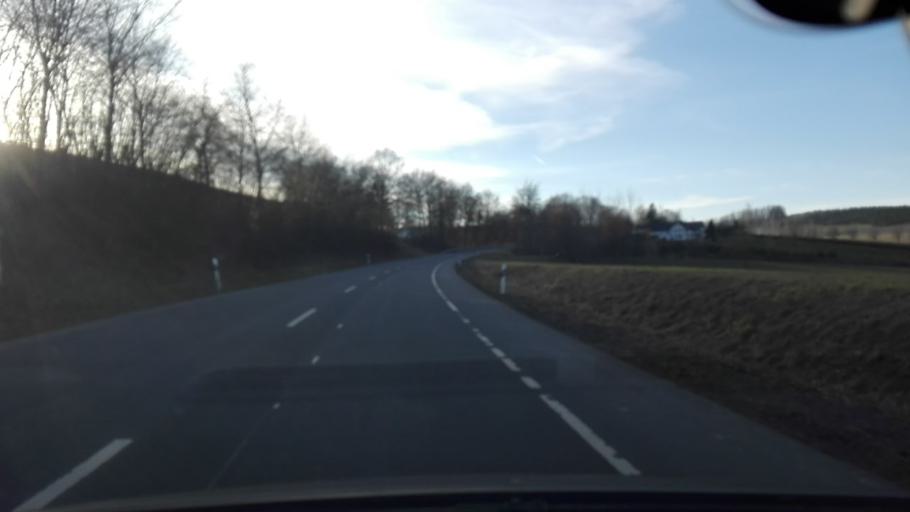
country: DE
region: North Rhine-Westphalia
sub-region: Regierungsbezirk Arnsberg
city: Schmallenberg
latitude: 51.1641
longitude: 8.2130
